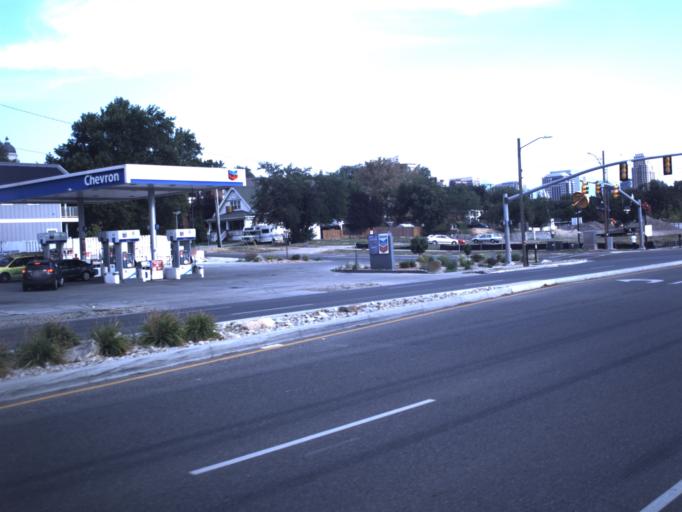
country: US
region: Utah
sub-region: Salt Lake County
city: Salt Lake City
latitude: 40.7831
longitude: -111.8998
